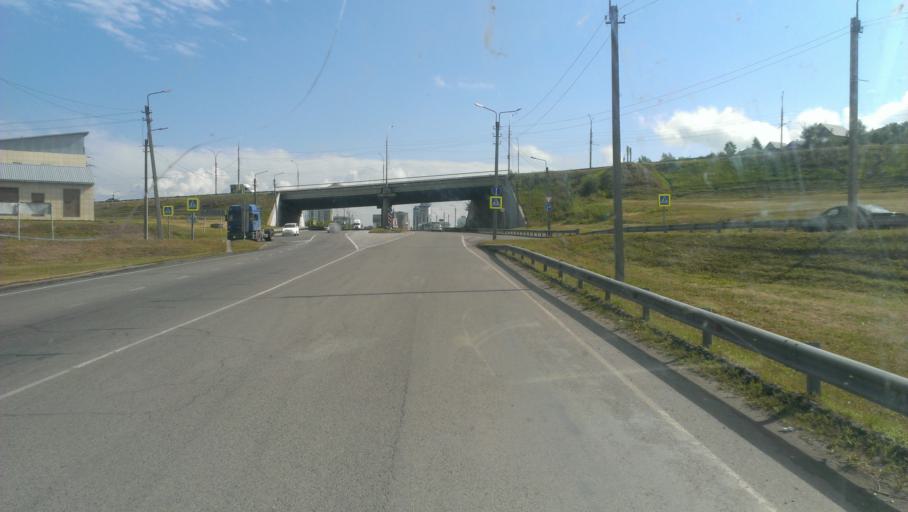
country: RU
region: Altai Krai
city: Zaton
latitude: 53.3226
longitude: 83.7854
